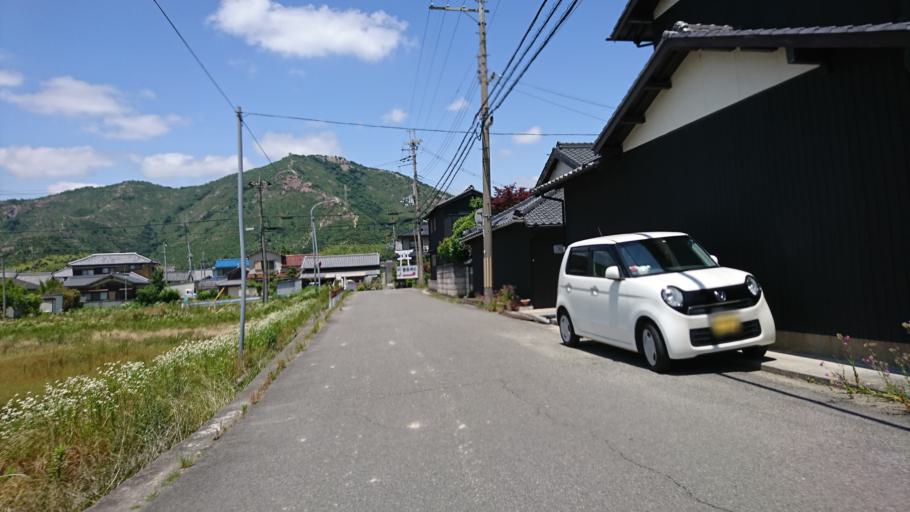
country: JP
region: Hyogo
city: Kakogawacho-honmachi
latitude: 34.8005
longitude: 134.7898
